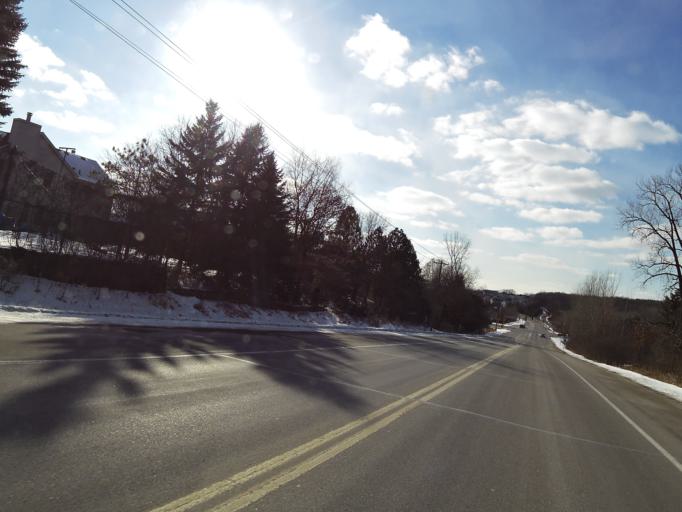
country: US
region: Minnesota
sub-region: Dakota County
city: Eagan
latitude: 44.7680
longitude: -93.1632
